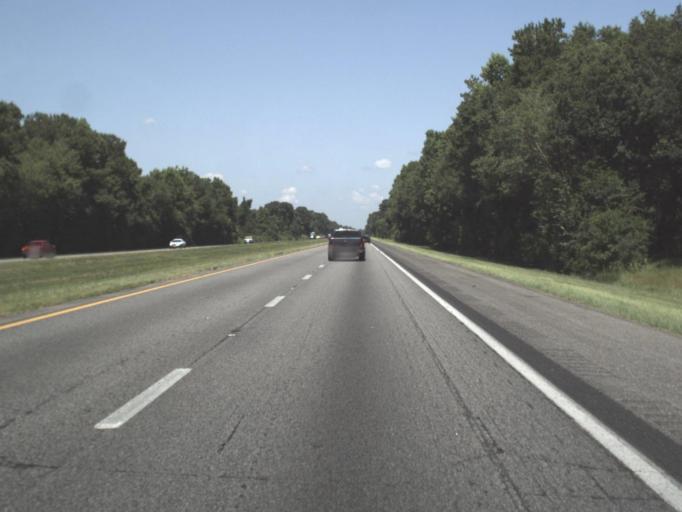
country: US
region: Florida
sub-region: Madison County
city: Madison
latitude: 30.4310
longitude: -83.5855
